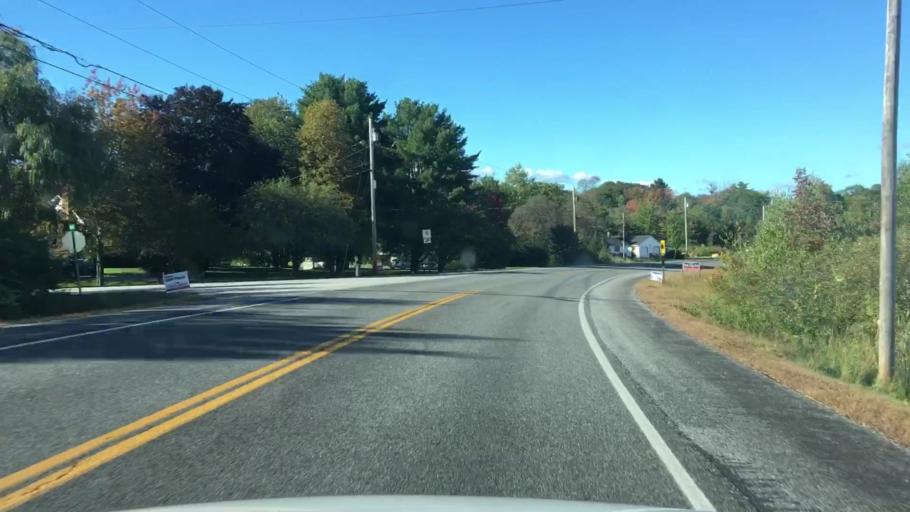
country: US
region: Maine
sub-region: Androscoggin County
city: Lisbon
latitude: 44.0569
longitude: -70.0862
